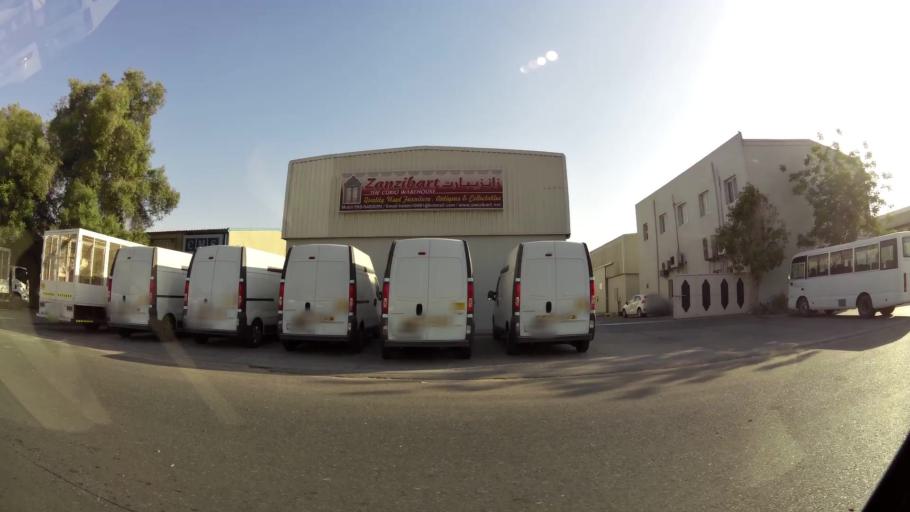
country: AE
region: Dubai
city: Dubai
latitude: 25.1261
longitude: 55.2427
